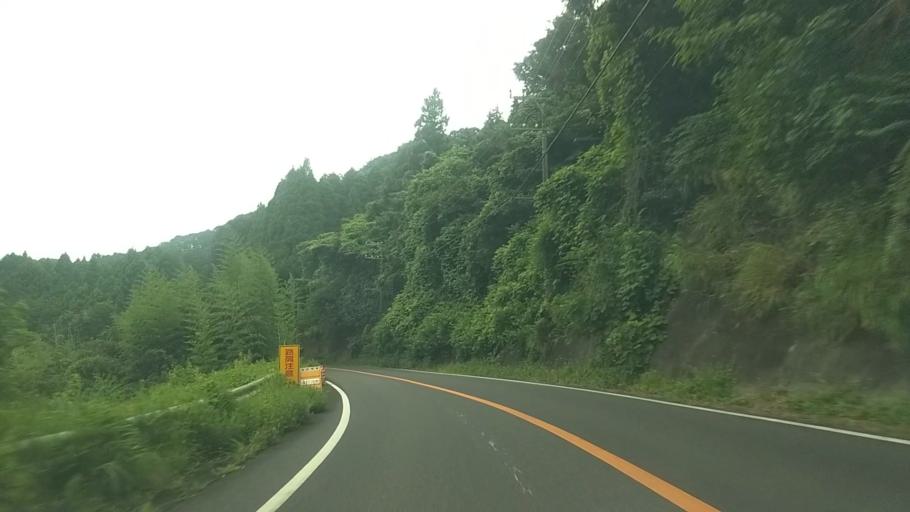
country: JP
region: Chiba
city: Kawaguchi
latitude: 35.2349
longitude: 140.0730
